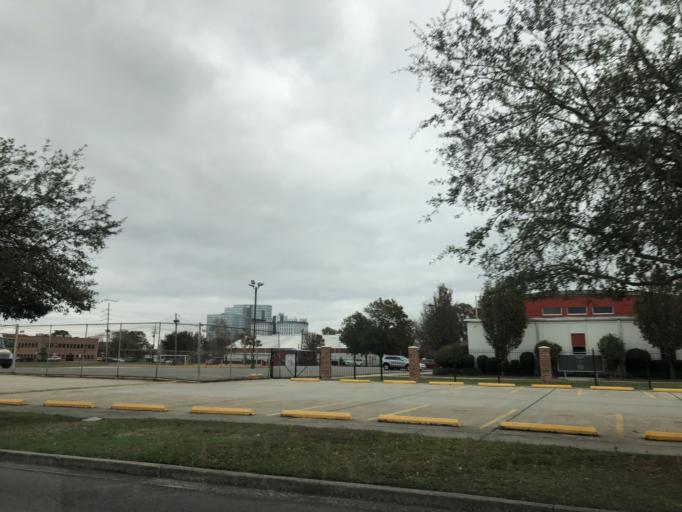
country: US
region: Louisiana
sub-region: Jefferson Parish
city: Metairie
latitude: 29.9912
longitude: -90.1601
